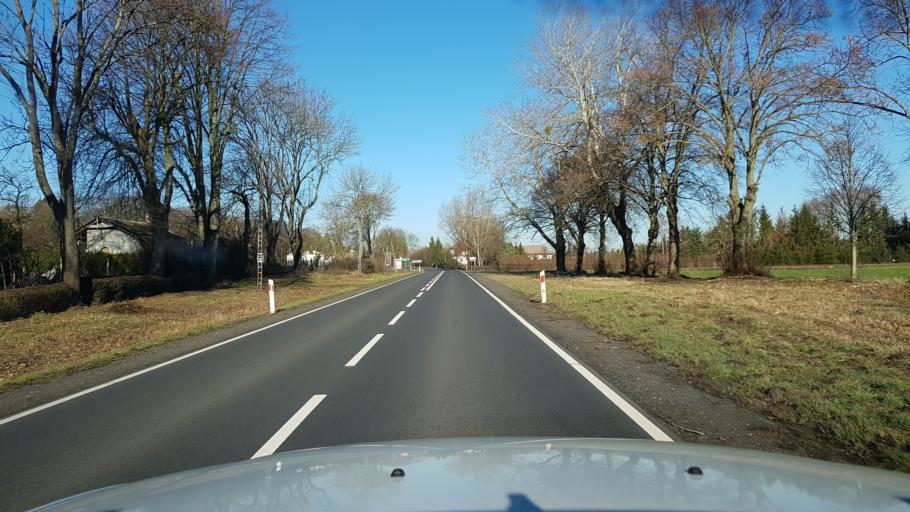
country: PL
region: West Pomeranian Voivodeship
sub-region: Powiat pyrzycki
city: Lipiany
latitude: 52.9974
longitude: 14.9801
